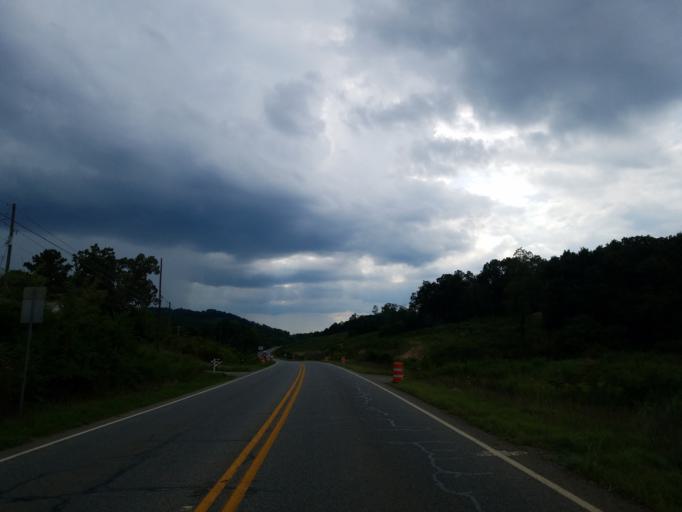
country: US
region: Georgia
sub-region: Bartow County
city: Adairsville
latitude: 34.3692
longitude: -85.0043
